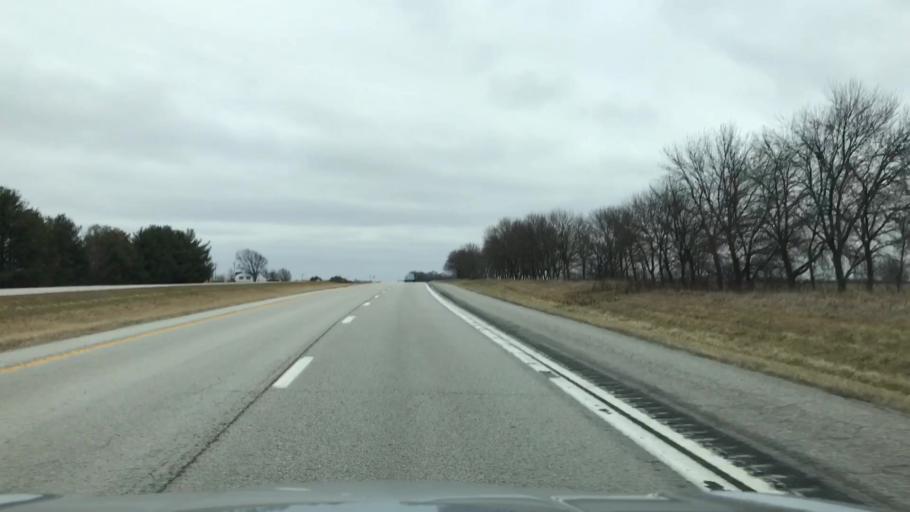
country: US
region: Missouri
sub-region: Livingston County
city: Chillicothe
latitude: 39.7771
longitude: -93.3810
